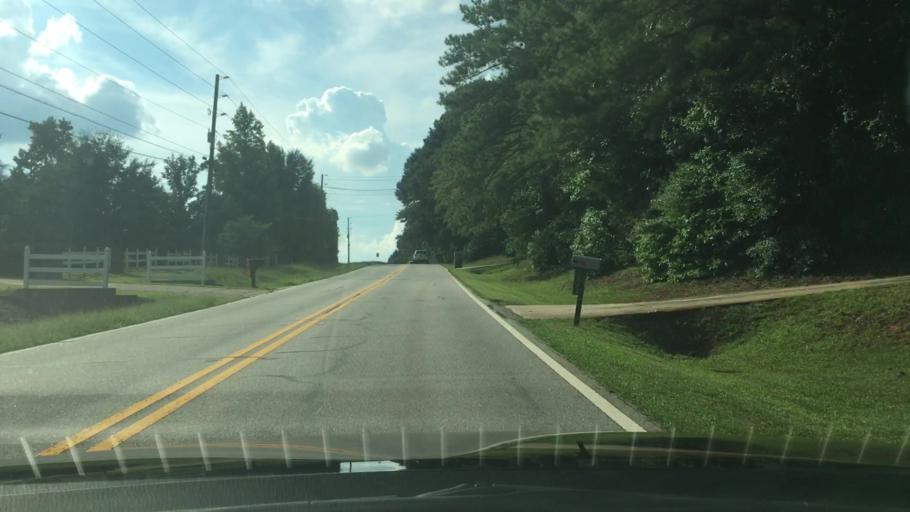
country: US
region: Georgia
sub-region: Coweta County
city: East Newnan
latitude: 33.3511
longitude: -84.6991
